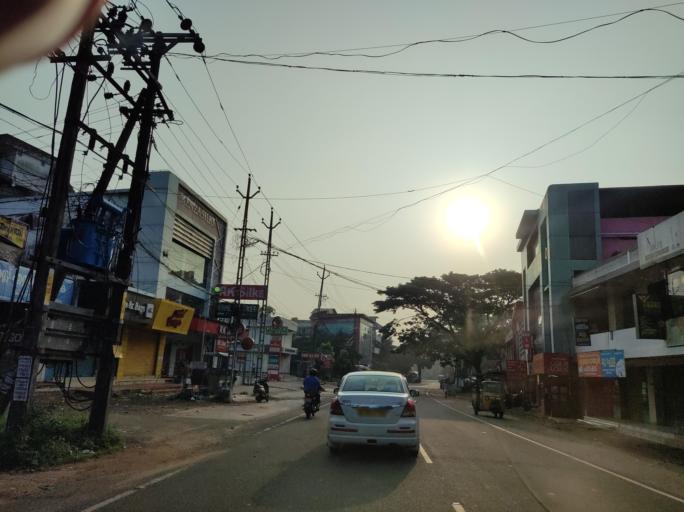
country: IN
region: Kerala
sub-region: Alappuzha
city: Kattanam
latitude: 9.1744
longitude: 76.6103
